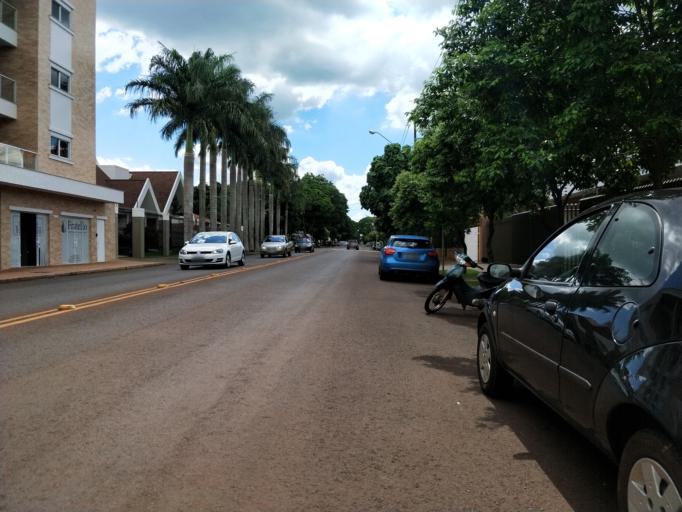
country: BR
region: Parana
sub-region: Marechal Candido Rondon
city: Marechal Candido Rondon
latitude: -24.5604
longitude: -54.0518
